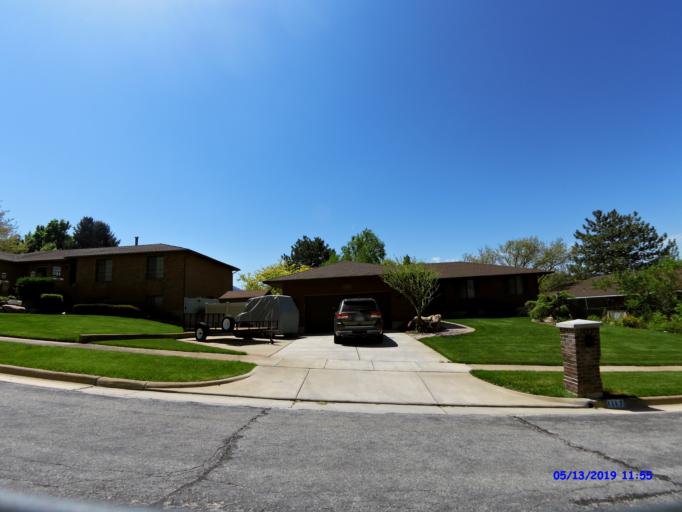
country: US
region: Utah
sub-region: Weber County
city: North Ogden
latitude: 41.2688
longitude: -111.9498
